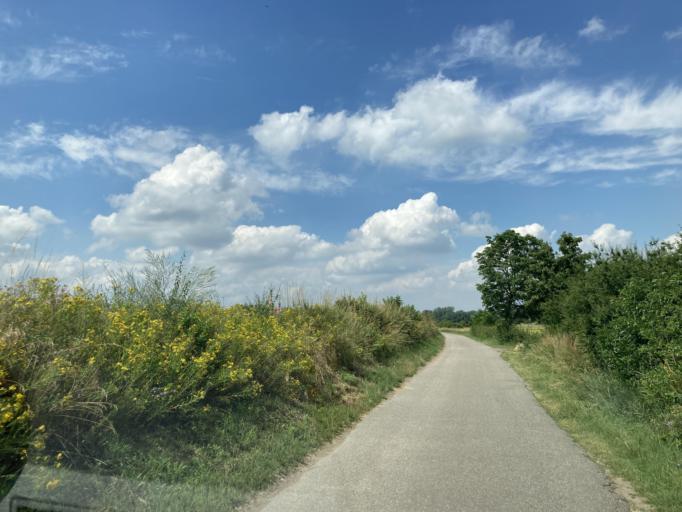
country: DE
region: Baden-Wuerttemberg
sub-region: Karlsruhe Region
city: Oberhausen-Rheinhausen
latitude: 49.2658
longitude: 8.4914
